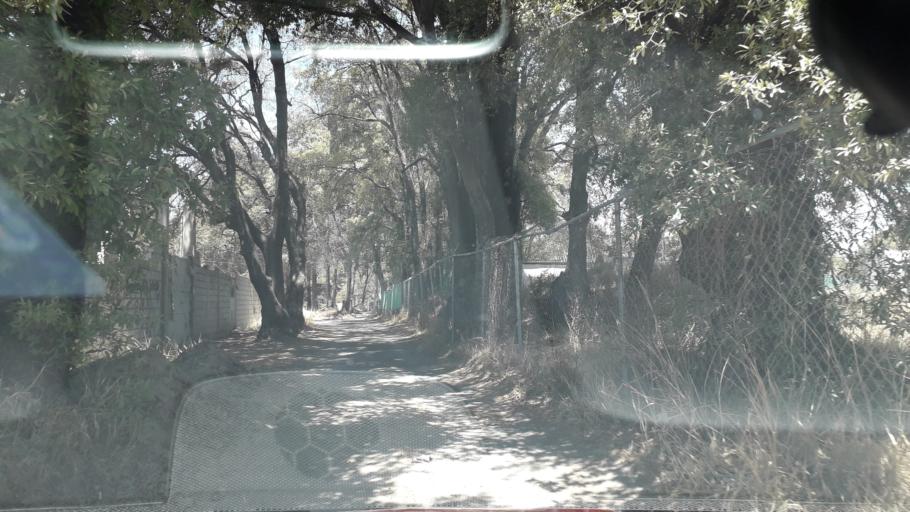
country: MX
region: Puebla
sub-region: Amozoc
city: Casa Blanca
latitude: 19.0587
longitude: -98.1148
